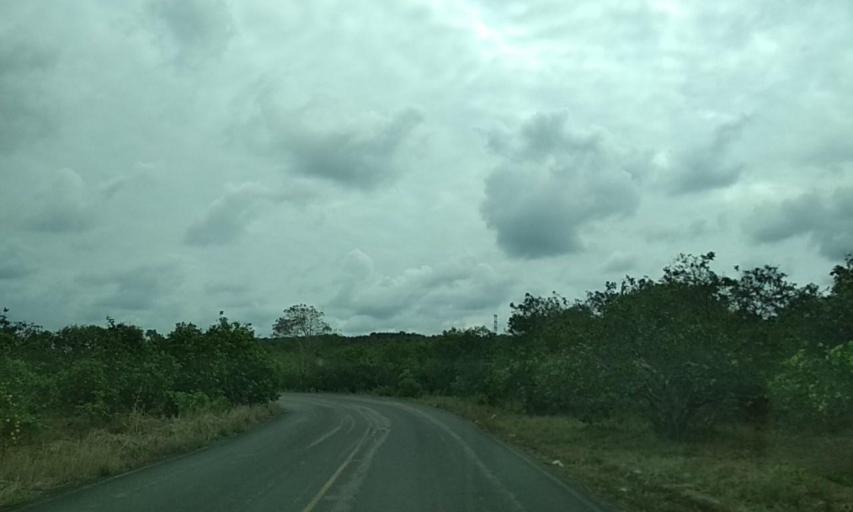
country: MX
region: Veracruz
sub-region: Papantla
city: El Chote
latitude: 20.3536
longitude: -97.3581
